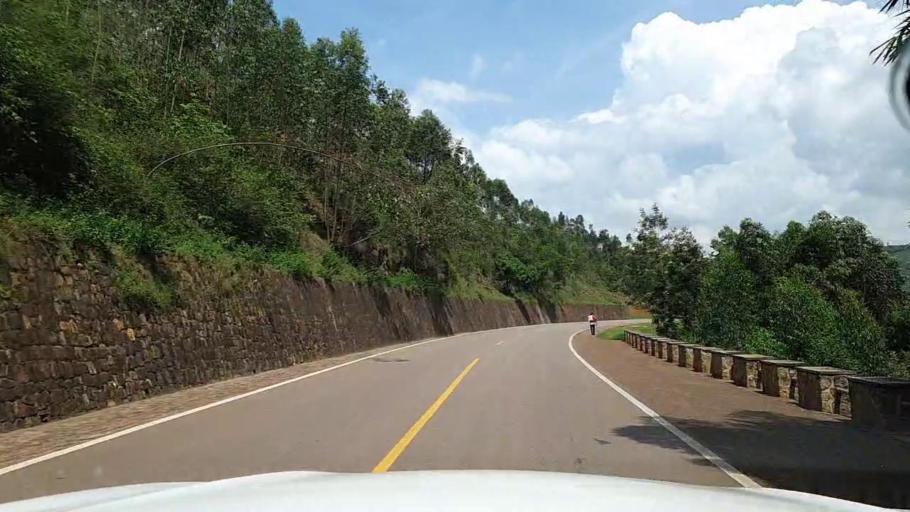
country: RW
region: Kigali
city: Kigali
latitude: -1.8292
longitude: 30.0788
